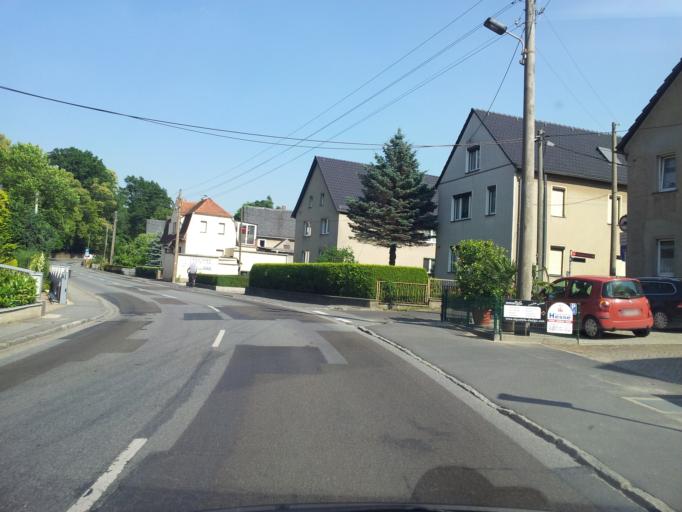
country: DE
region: Saxony
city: Wachau
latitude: 51.1589
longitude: 13.8807
